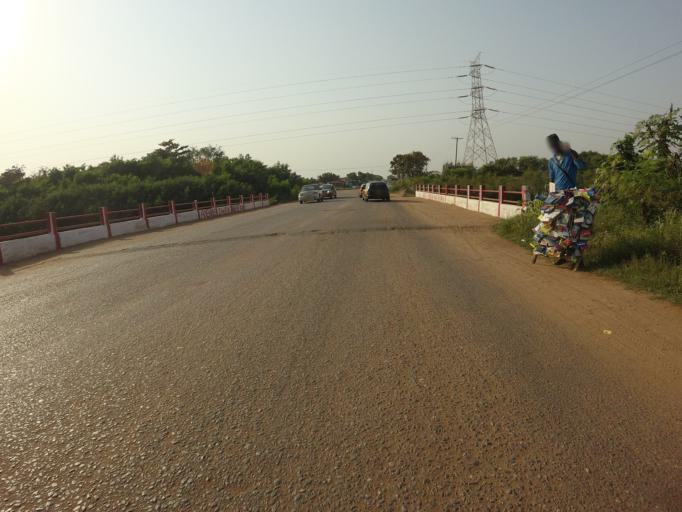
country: GH
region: Greater Accra
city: Tema
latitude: 5.6930
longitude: 0.0508
